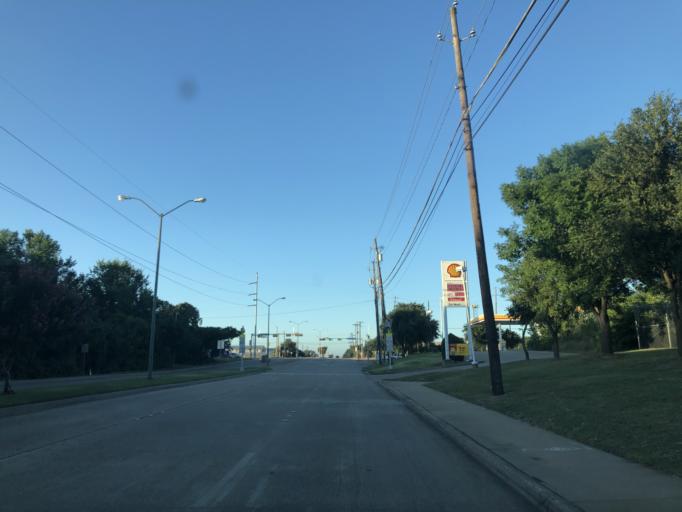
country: US
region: Texas
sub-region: Dallas County
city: Duncanville
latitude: 32.6641
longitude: -96.9259
